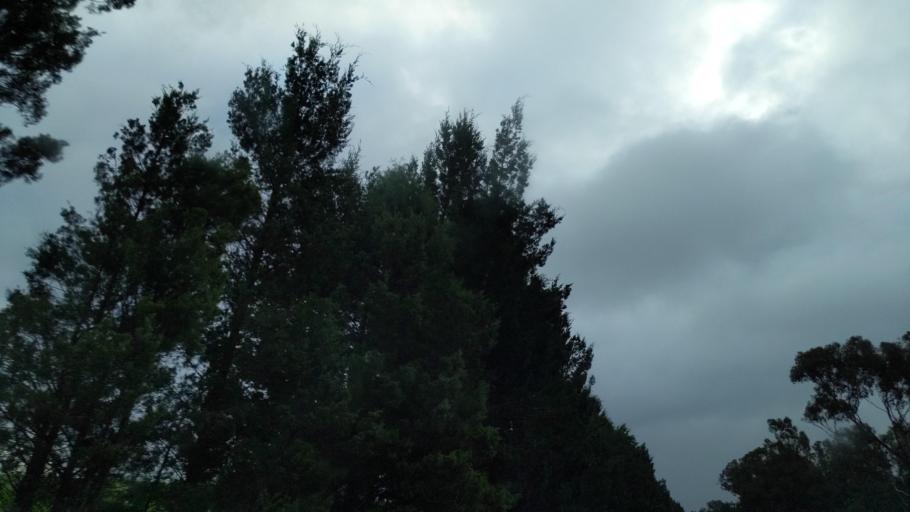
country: AU
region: New South Wales
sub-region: Coolamon
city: Coolamon
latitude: -34.9484
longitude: 147.3121
